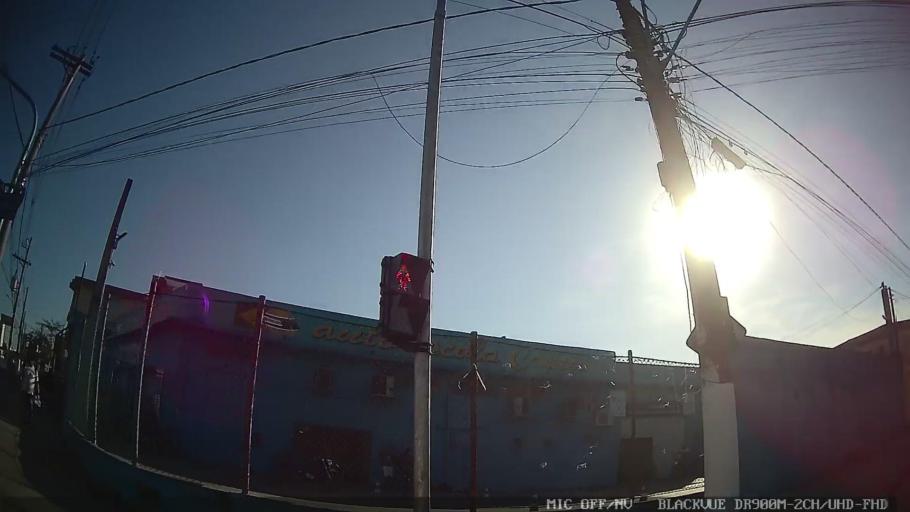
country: BR
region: Sao Paulo
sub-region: Guaruja
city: Guaruja
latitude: -23.9770
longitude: -46.2228
